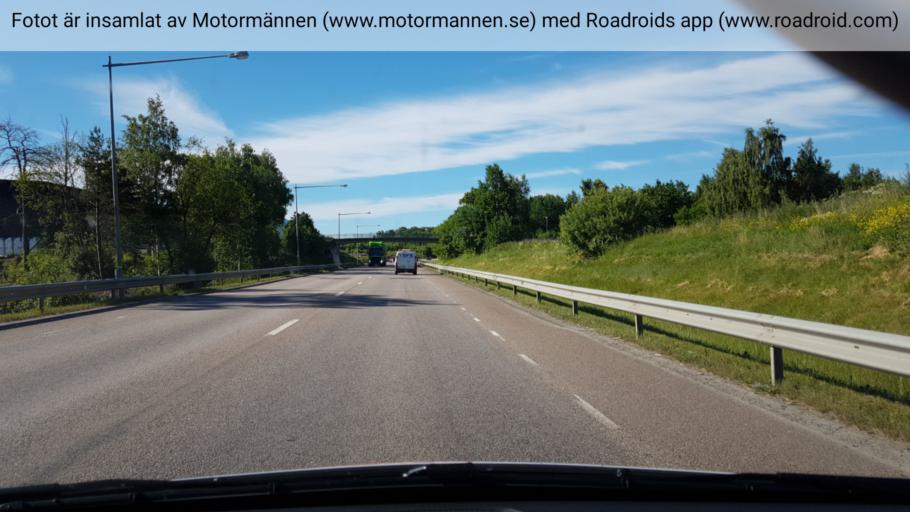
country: SE
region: Vaestra Goetaland
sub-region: Skovde Kommun
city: Skoevde
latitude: 58.3876
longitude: 13.8748
